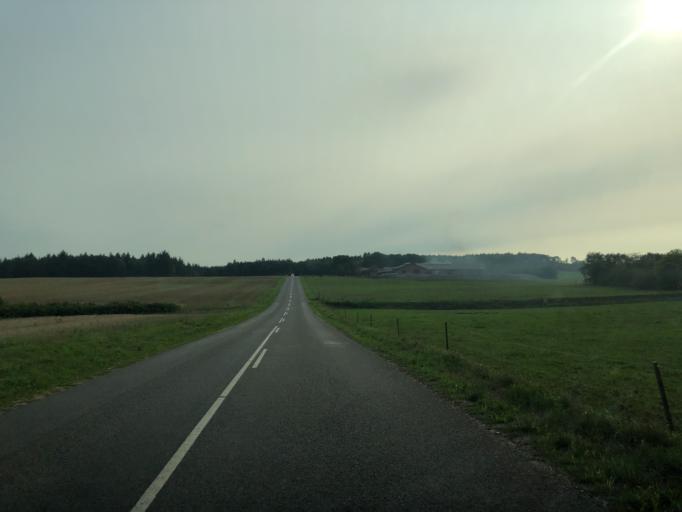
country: DK
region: Central Jutland
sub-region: Ringkobing-Skjern Kommune
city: Videbaek
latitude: 56.0691
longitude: 8.6956
